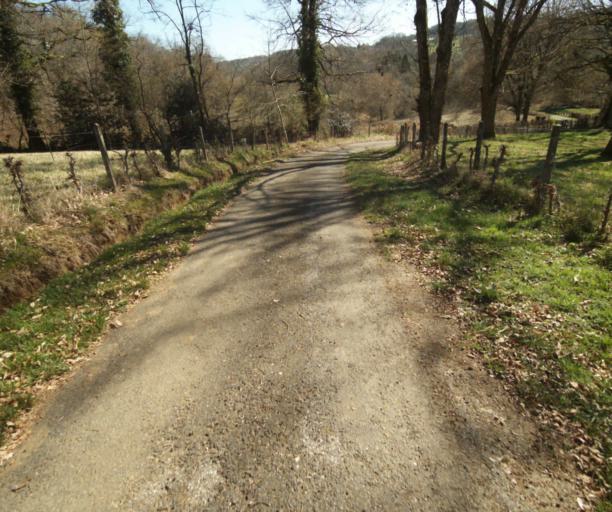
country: FR
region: Limousin
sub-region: Departement de la Correze
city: Chamboulive
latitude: 45.4068
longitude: 1.6418
